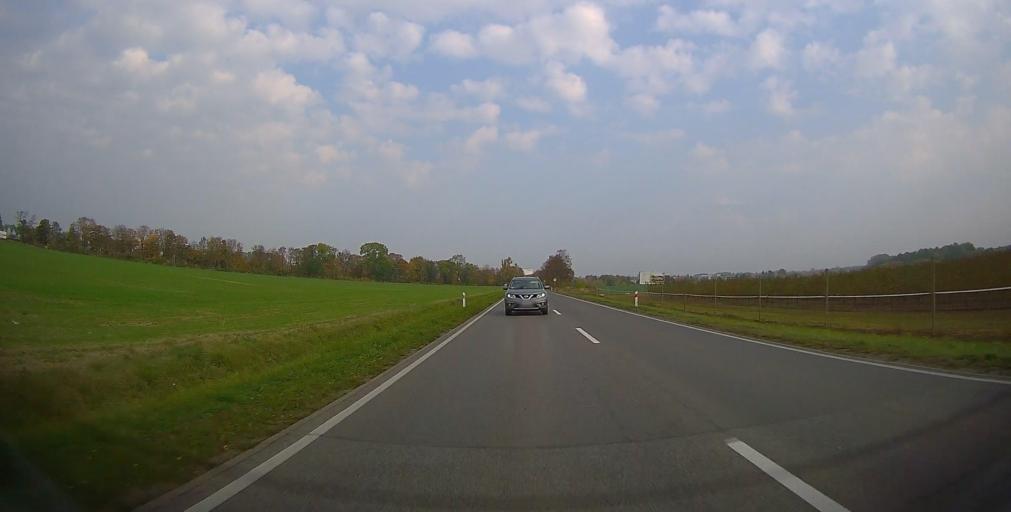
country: PL
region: Masovian Voivodeship
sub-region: Powiat grojecki
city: Belsk Duzy
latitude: 51.8064
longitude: 20.7923
